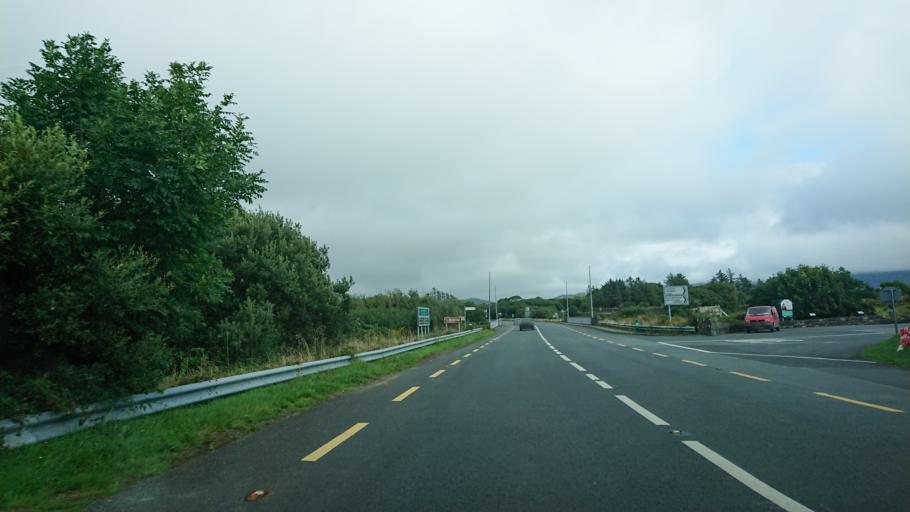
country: IE
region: Munster
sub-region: Ciarrai
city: Cahersiveen
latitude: 51.9518
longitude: -10.2055
